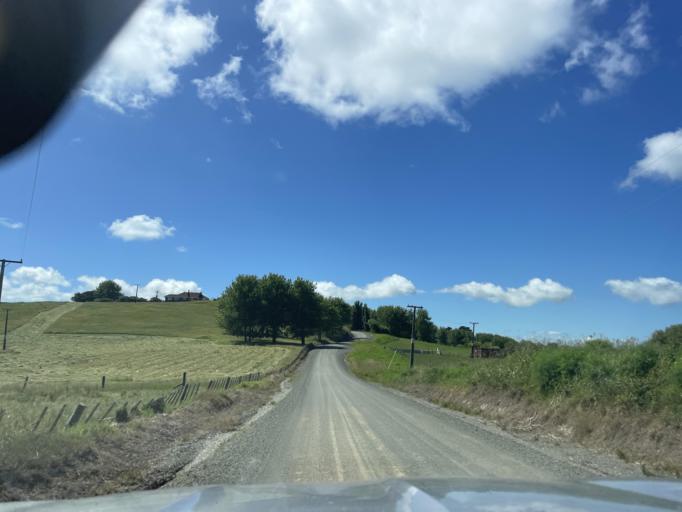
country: NZ
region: Auckland
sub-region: Auckland
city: Wellsford
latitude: -36.2564
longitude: 174.3669
